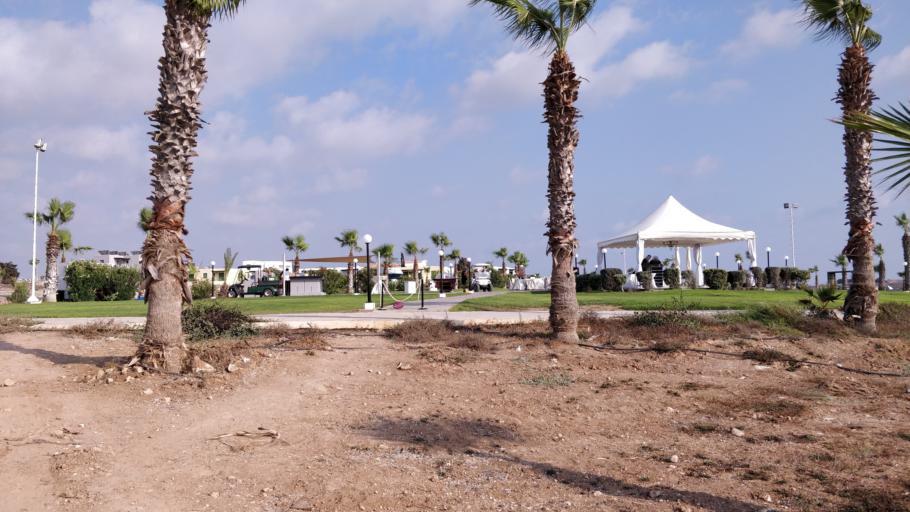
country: CY
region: Pafos
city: Paphos
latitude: 34.7714
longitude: 32.4043
